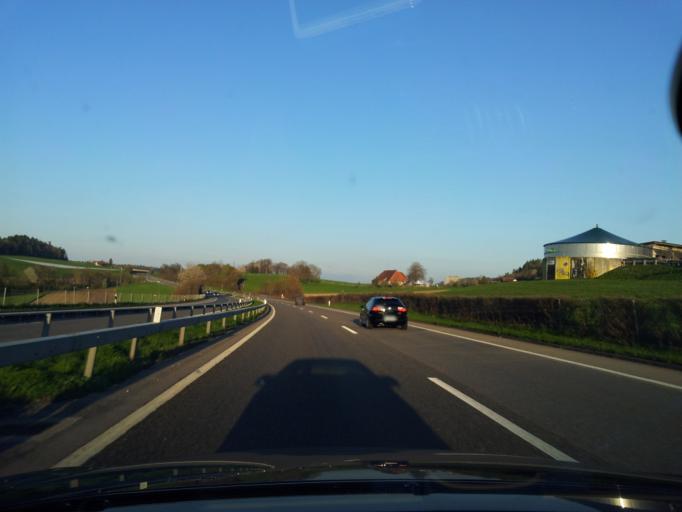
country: CH
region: Bern
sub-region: Seeland District
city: Grossaffoltern
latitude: 47.0482
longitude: 7.3487
